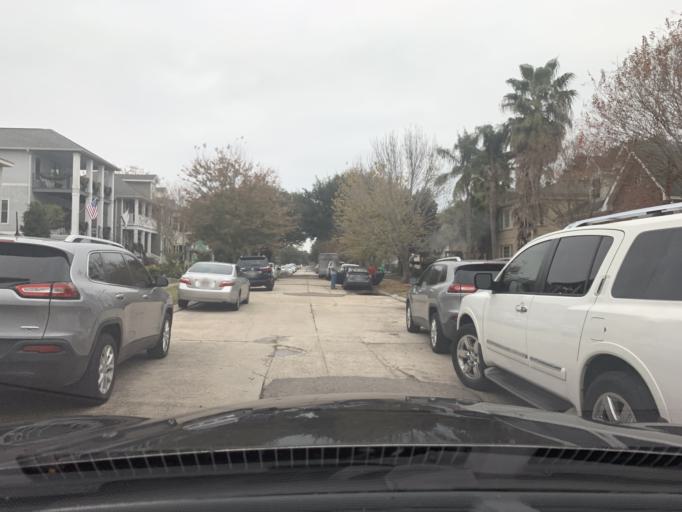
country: US
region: Louisiana
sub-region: Jefferson Parish
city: Metairie
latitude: 30.0143
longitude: -90.1082
